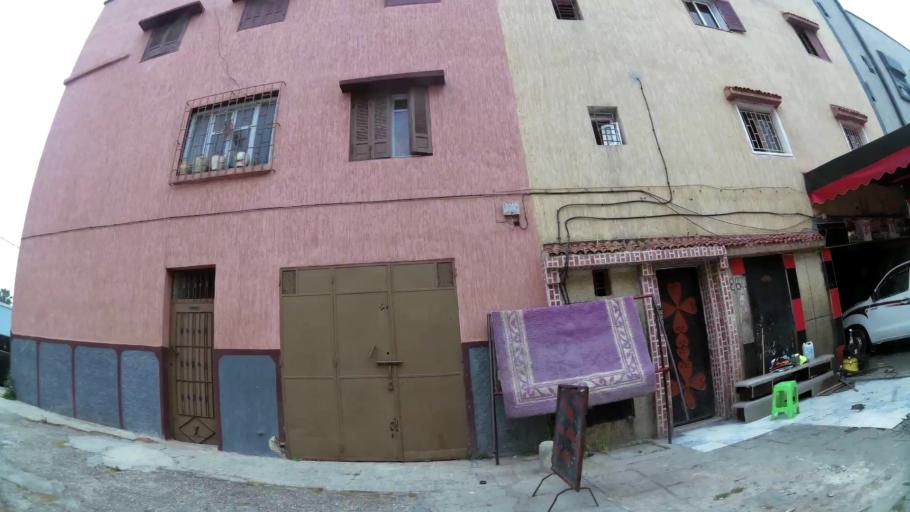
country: MA
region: Rabat-Sale-Zemmour-Zaer
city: Sale
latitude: 34.0466
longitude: -6.7999
